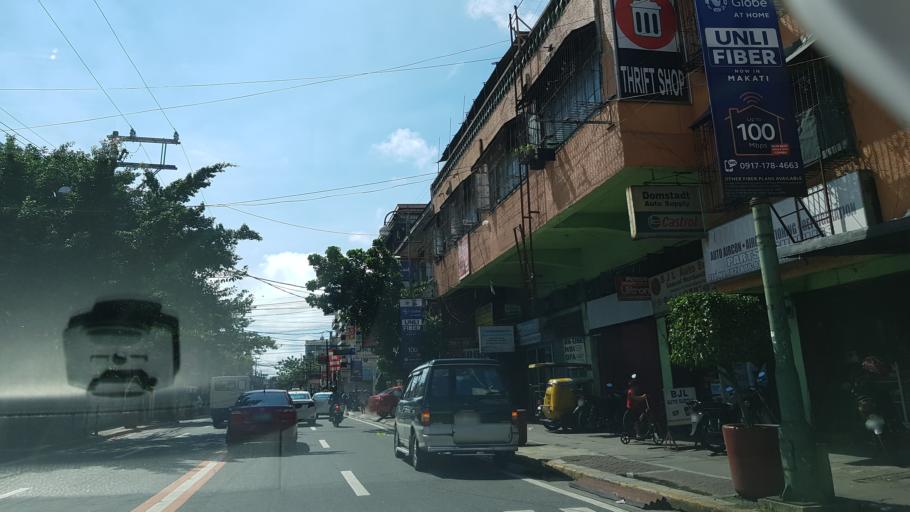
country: PH
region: Metro Manila
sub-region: Makati City
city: Makati City
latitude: 14.5701
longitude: 121.0231
